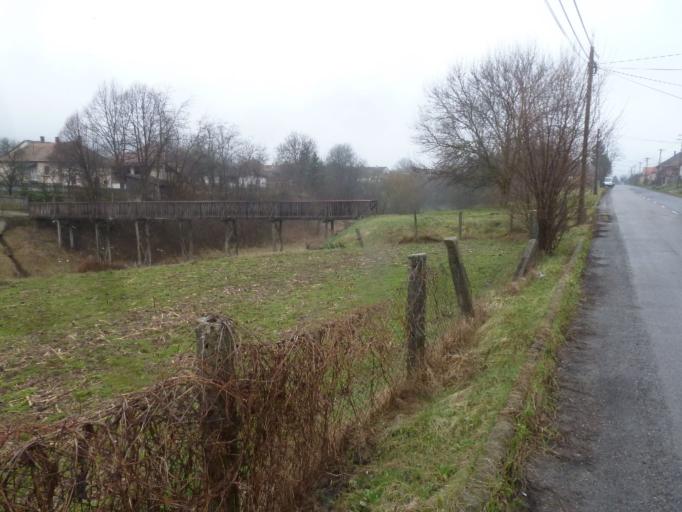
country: HU
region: Nograd
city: Matranovak
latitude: 48.1486
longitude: 19.9570
